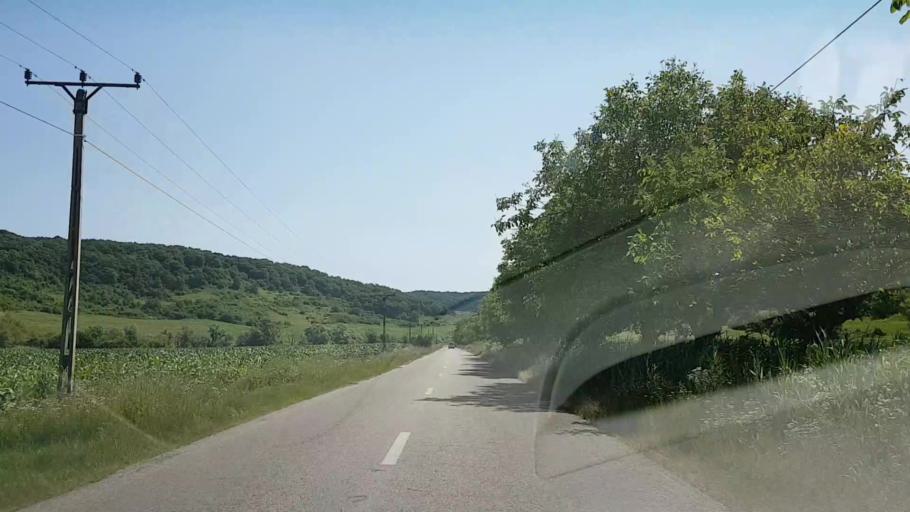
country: RO
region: Mures
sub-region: Comuna Apold
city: Apold
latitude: 46.1425
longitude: 24.8061
